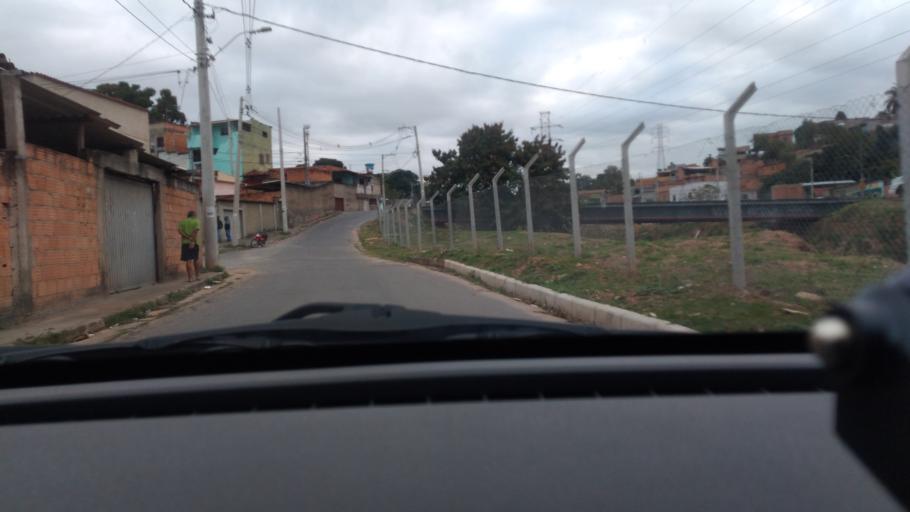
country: BR
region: Minas Gerais
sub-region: Belo Horizonte
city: Belo Horizonte
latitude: -19.8226
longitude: -43.9378
